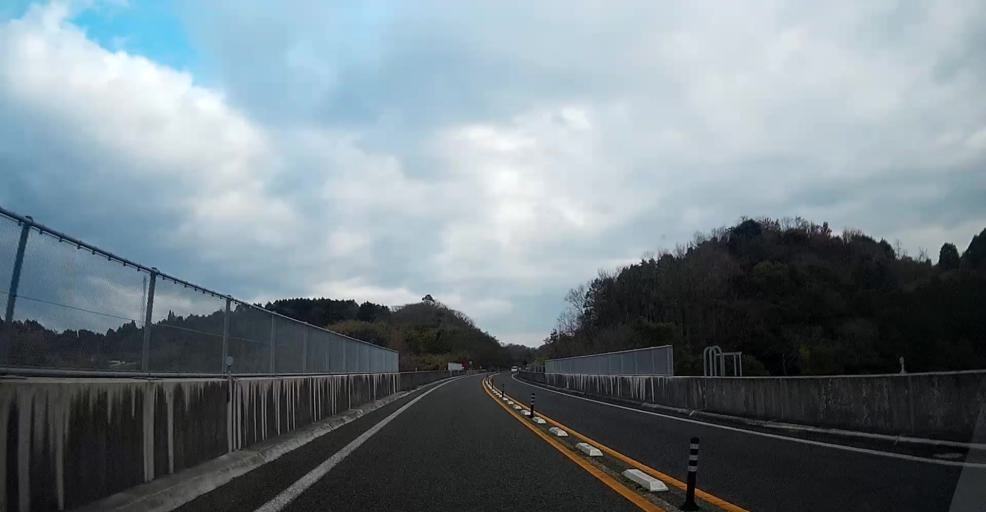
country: JP
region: Kumamoto
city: Hondo
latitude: 32.5097
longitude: 130.3194
